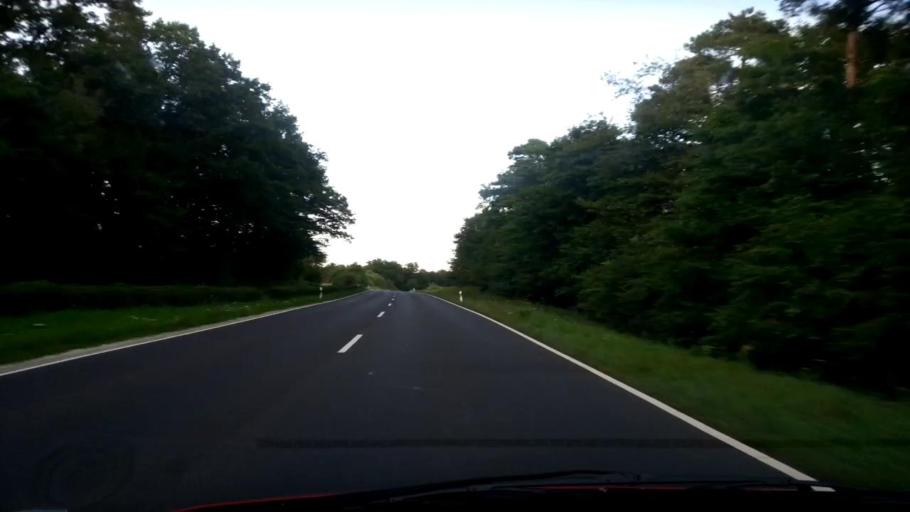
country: DE
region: Bavaria
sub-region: Upper Franconia
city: Stegaurach
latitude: 49.8368
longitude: 10.8175
